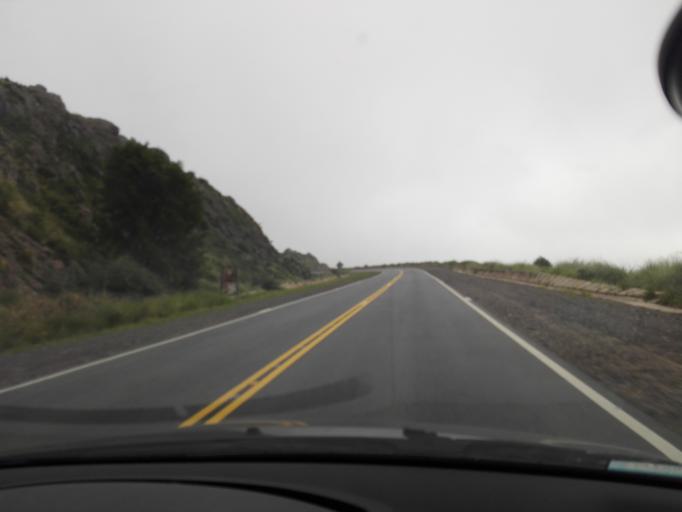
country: AR
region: Cordoba
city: Cuesta Blanca
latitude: -31.6126
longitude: -64.6926
